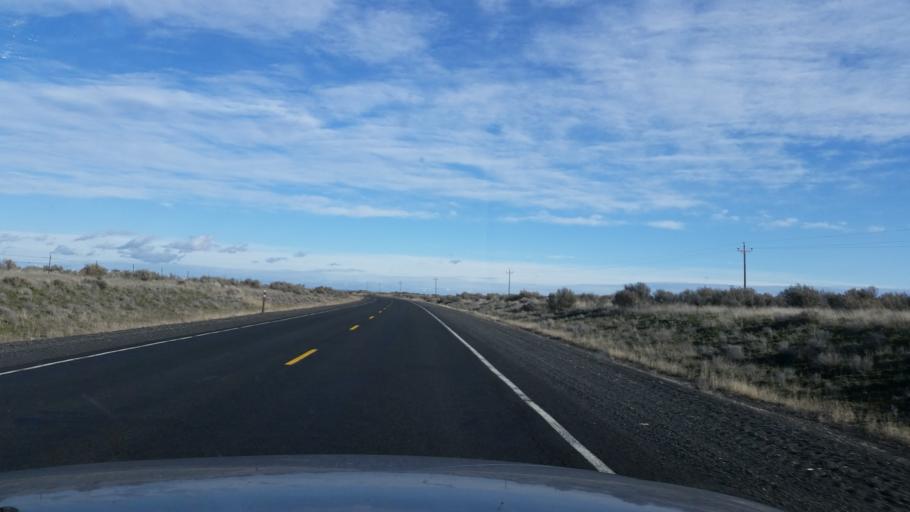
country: US
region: Washington
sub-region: Adams County
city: Ritzville
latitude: 47.3140
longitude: -118.7524
